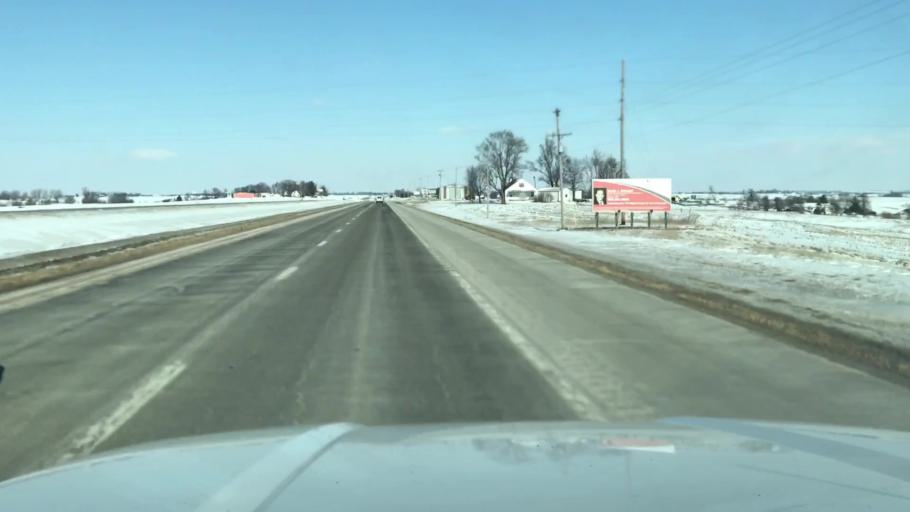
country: US
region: Missouri
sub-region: Nodaway County
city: Maryville
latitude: 40.2813
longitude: -94.8755
